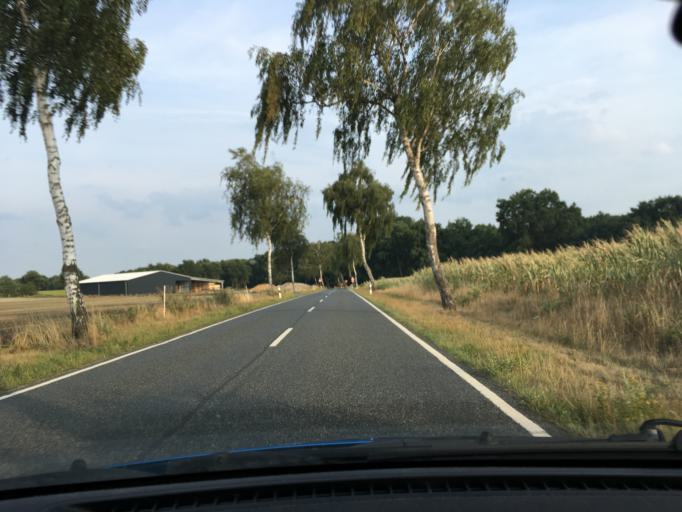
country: DE
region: Lower Saxony
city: Toppenstedt
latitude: 53.3038
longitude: 10.0881
